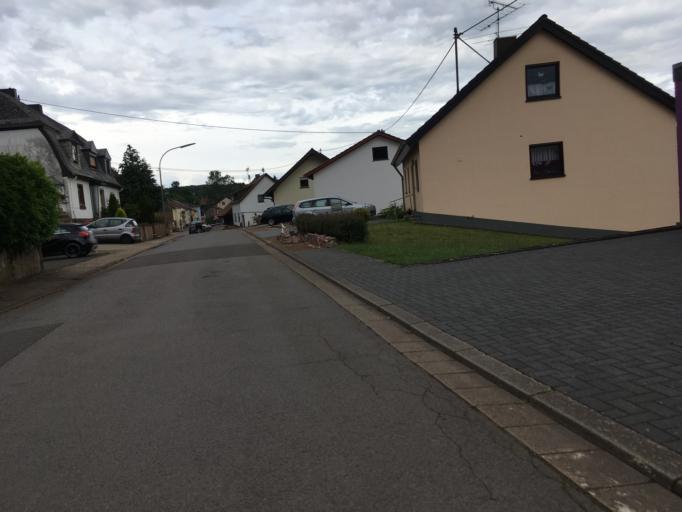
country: DE
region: Saarland
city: Britten
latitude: 49.5084
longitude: 6.6794
